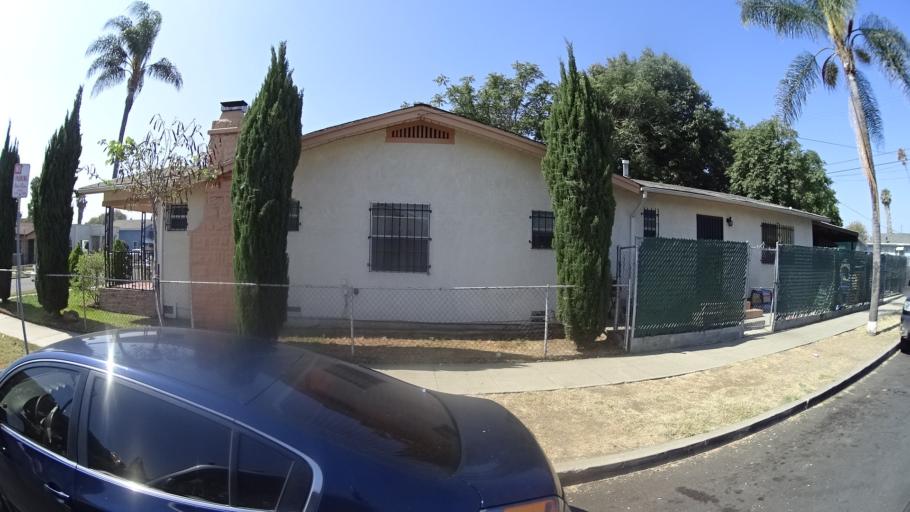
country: US
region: California
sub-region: Los Angeles County
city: View Park-Windsor Hills
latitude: 33.9818
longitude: -118.3249
